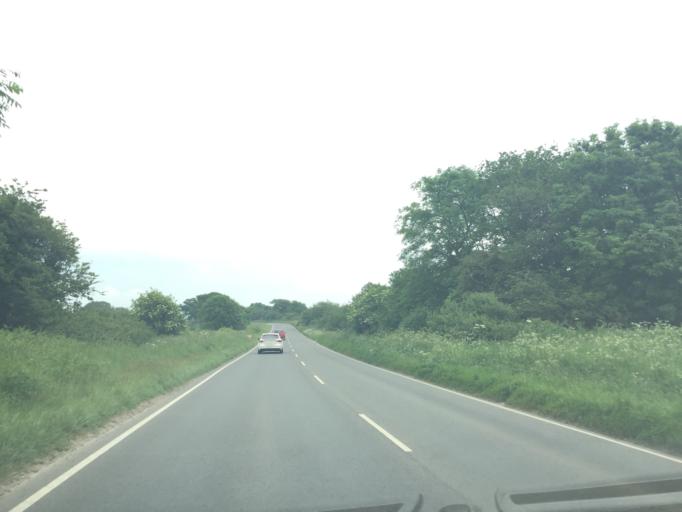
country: GB
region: England
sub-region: Dorset
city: Bovington Camp
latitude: 50.6633
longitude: -2.3004
